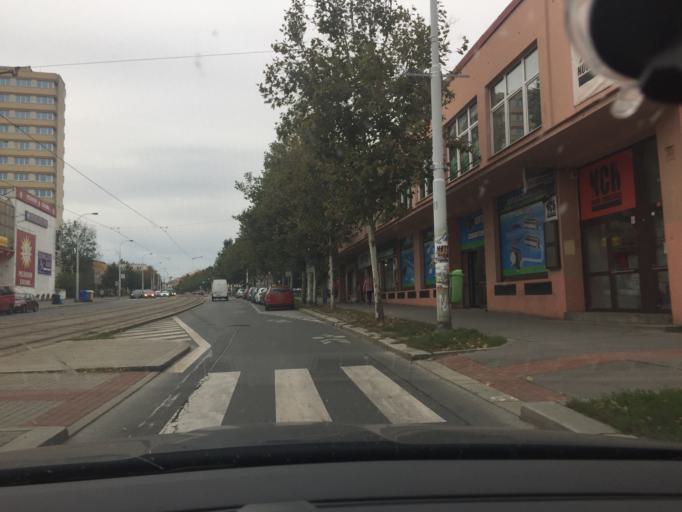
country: CZ
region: Praha
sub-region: Praha 8
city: Liben
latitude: 50.0925
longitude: 14.4904
